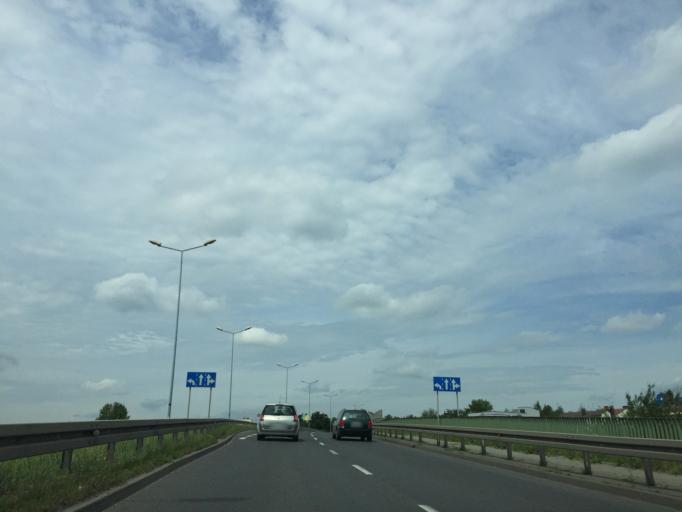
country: PL
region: Lesser Poland Voivodeship
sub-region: Powiat olkuski
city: Olkusz
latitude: 50.2727
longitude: 19.5865
